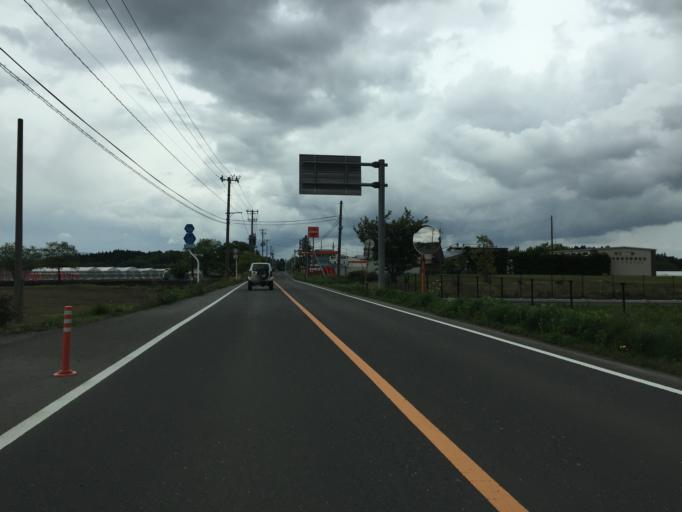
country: JP
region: Fukushima
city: Ishikawa
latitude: 37.1951
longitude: 140.3760
